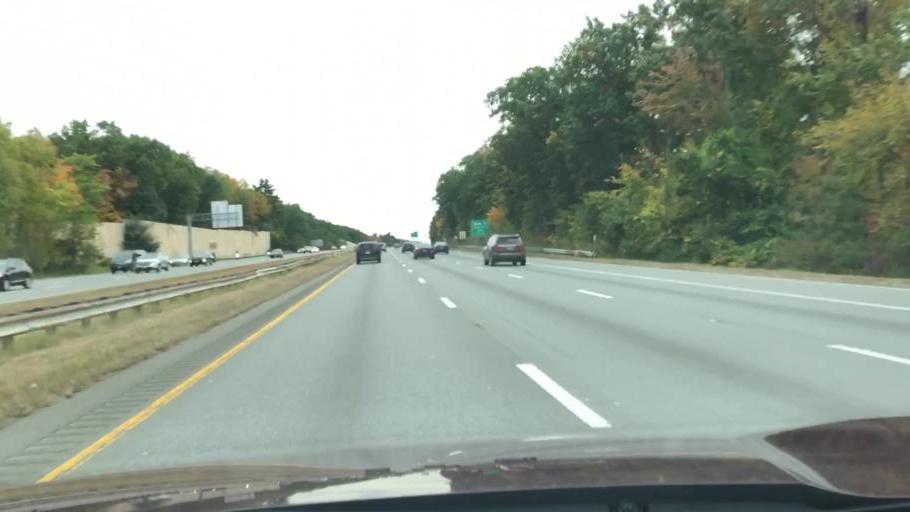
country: US
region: Massachusetts
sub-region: Essex County
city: Andover
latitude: 42.6382
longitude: -71.1826
